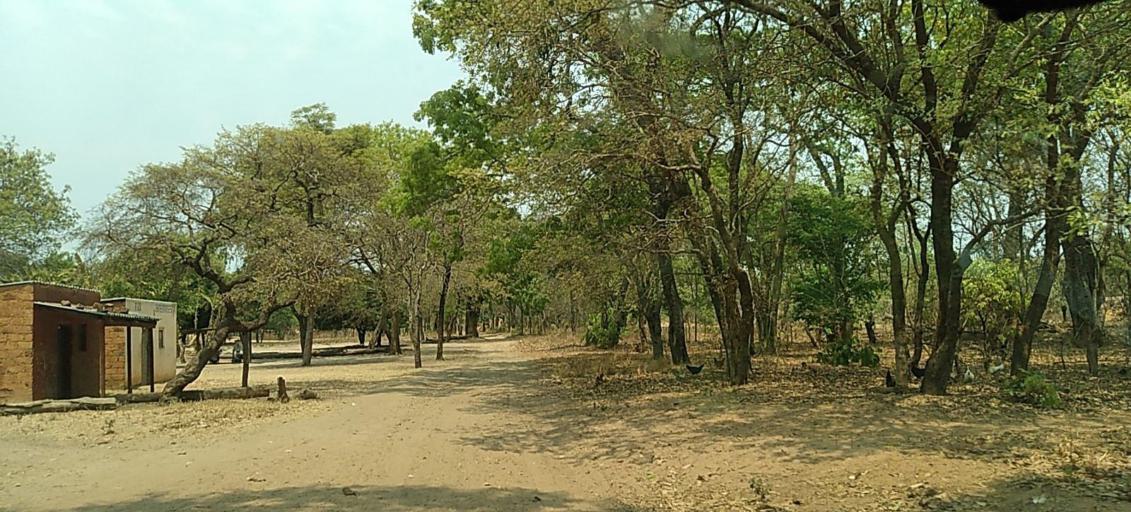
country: ZM
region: North-Western
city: Kabompo
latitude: -13.5644
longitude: 24.4443
